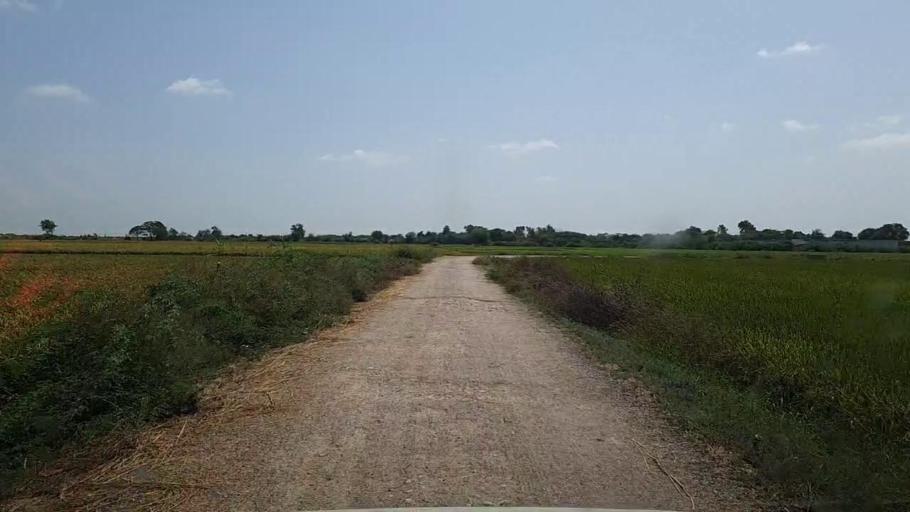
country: PK
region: Sindh
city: Kario
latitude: 24.6352
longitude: 68.5719
